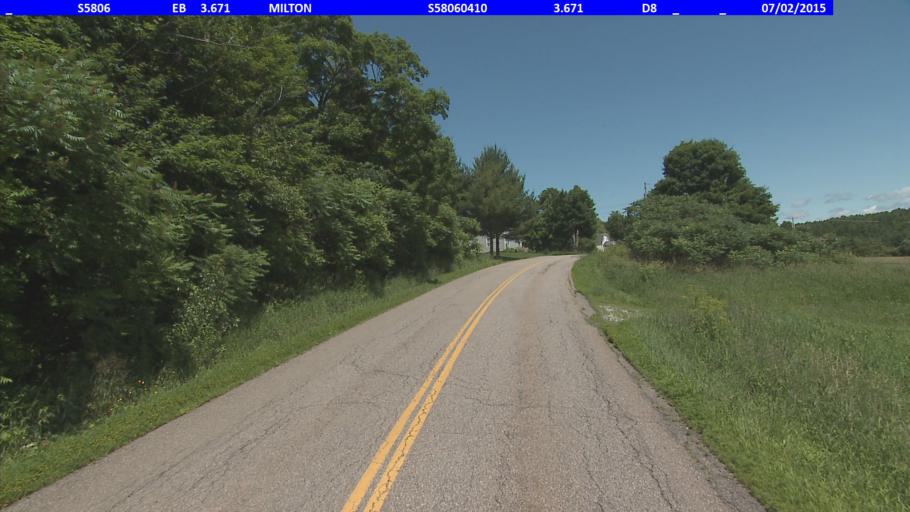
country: US
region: Vermont
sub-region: Chittenden County
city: Milton
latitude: 44.6745
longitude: -73.1761
